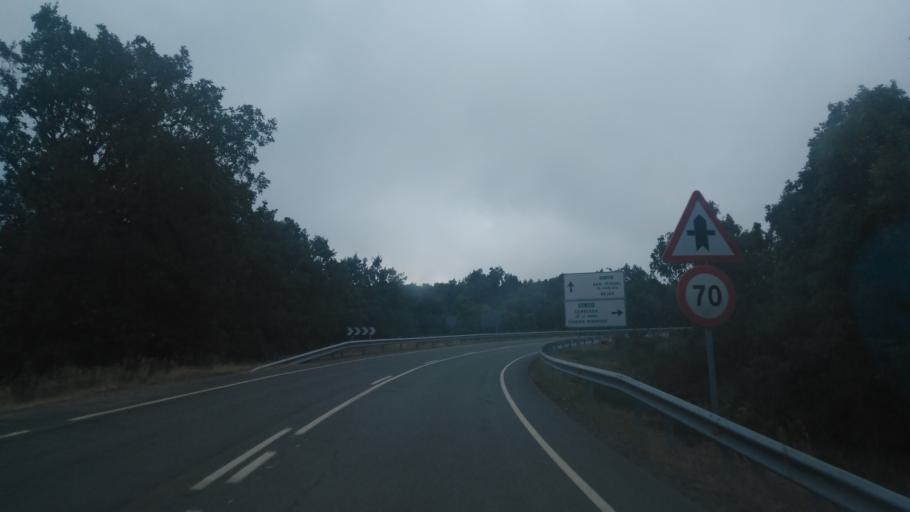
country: ES
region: Castille and Leon
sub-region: Provincia de Salamanca
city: Cilleros de la Bastida
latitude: 40.5589
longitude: -6.0676
